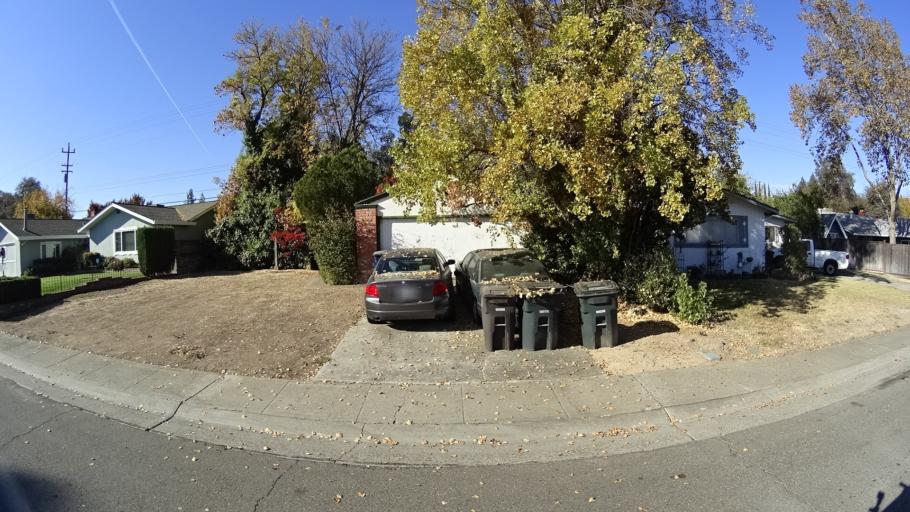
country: US
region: California
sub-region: Sacramento County
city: Antelope
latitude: 38.7131
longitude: -121.3084
